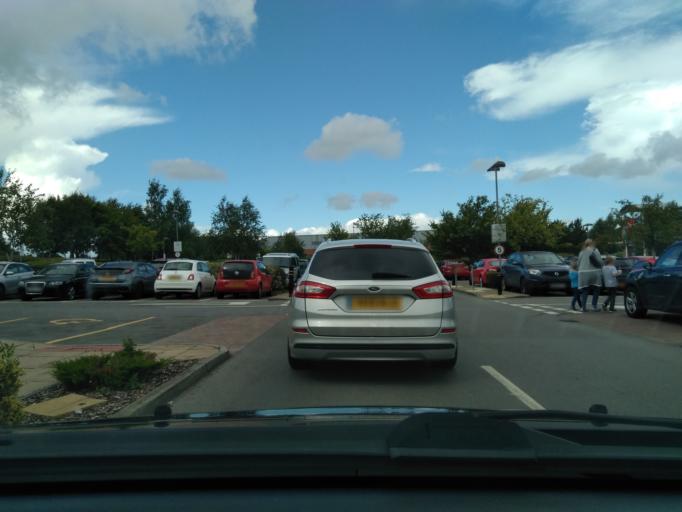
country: GB
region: England
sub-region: North Yorkshire
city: Knaresborough
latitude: 53.9996
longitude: -1.4444
